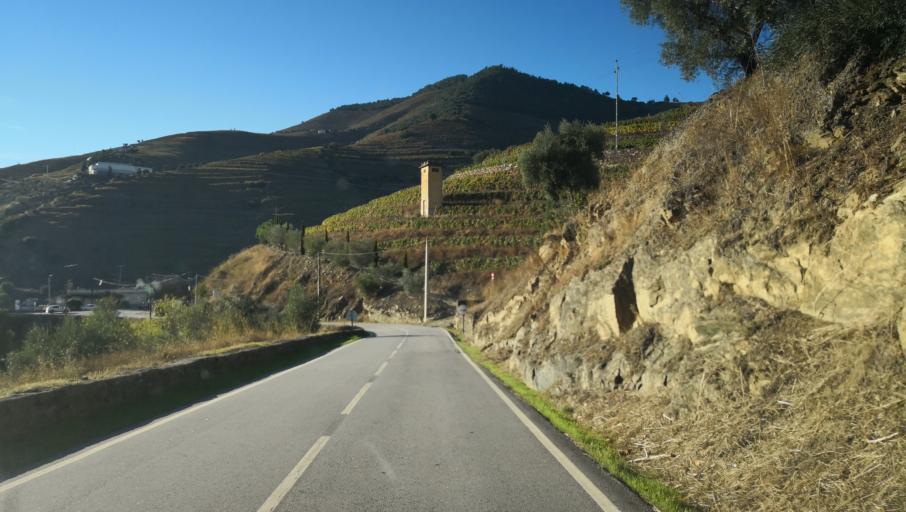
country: PT
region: Viseu
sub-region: Tabuaco
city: Tabuaco
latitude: 41.1744
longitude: -7.5508
